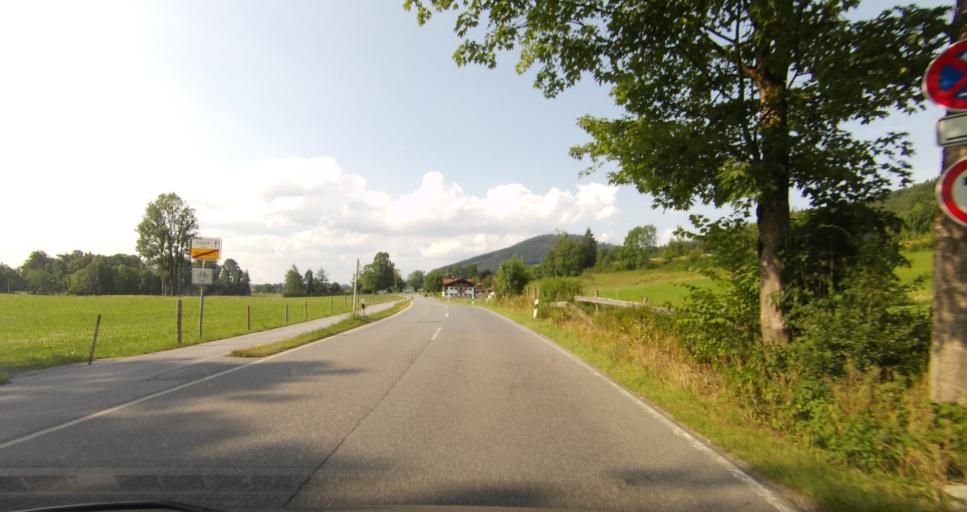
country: DE
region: Bavaria
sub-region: Upper Bavaria
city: Fischbachau
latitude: 47.7269
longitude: 11.9533
